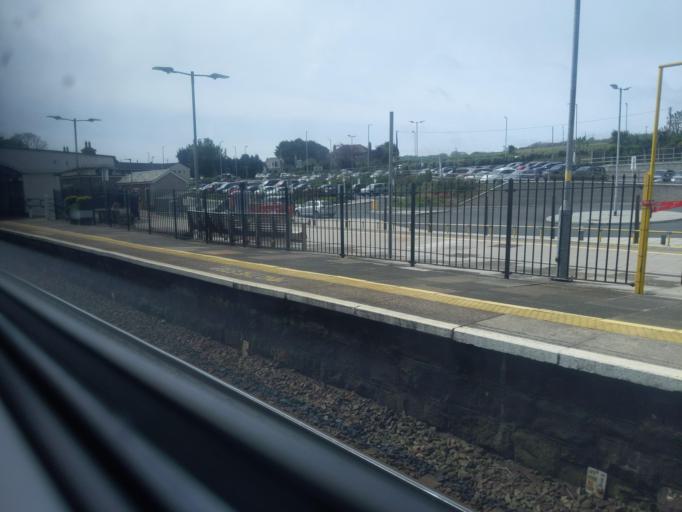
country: GB
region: England
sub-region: Cornwall
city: Hayle
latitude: 50.1708
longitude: -5.4433
